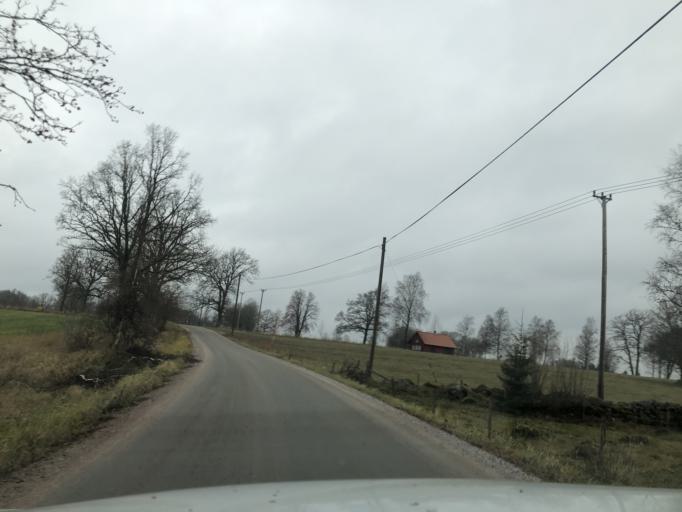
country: SE
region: Vaestra Goetaland
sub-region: Ulricehamns Kommun
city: Ulricehamn
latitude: 57.8617
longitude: 13.5935
